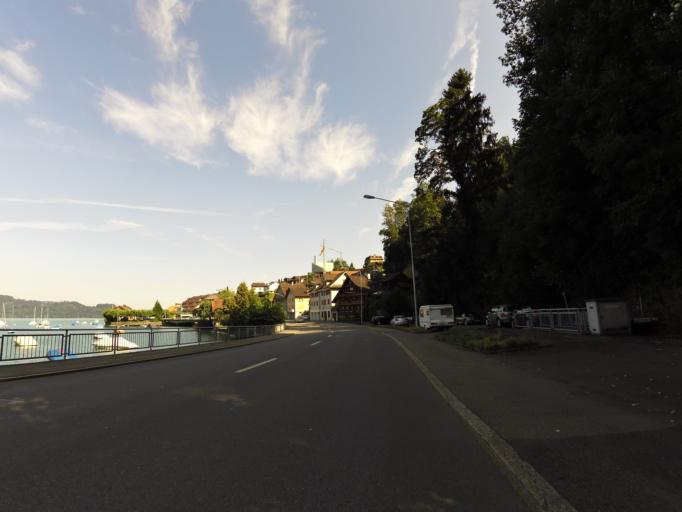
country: CH
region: Zug
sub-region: Zug
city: Walchwil
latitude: 47.0941
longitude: 8.5195
